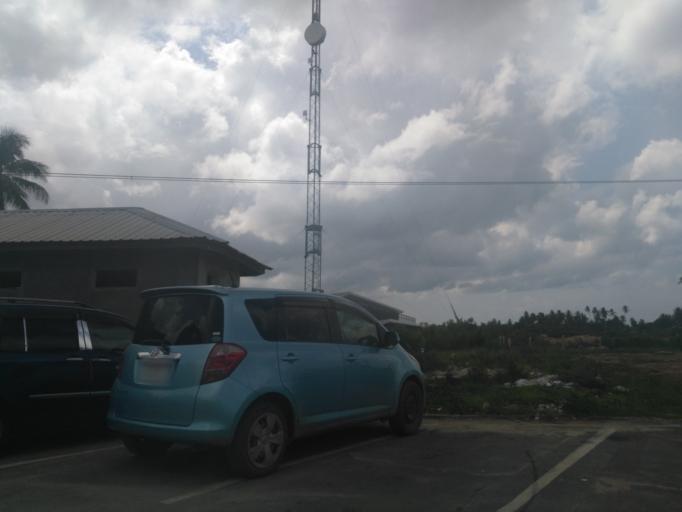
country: TZ
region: Zanzibar Urban/West
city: Zanzibar
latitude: -6.2190
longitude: 39.2207
